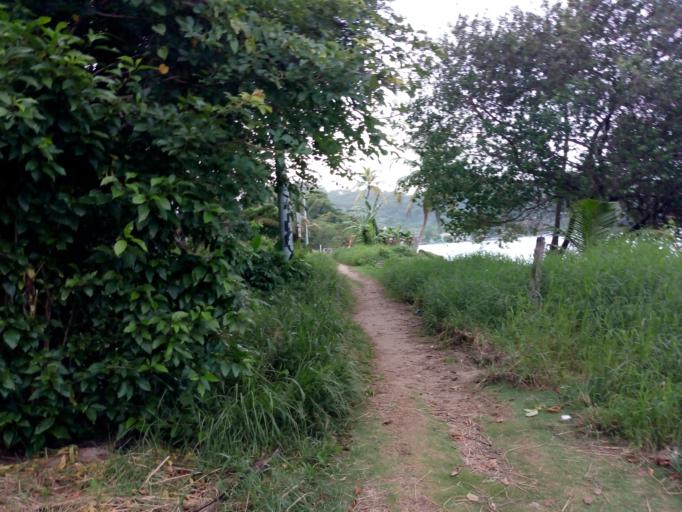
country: PA
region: Guna Yala
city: Puerto Obaldia
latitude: 8.6565
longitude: -77.3657
